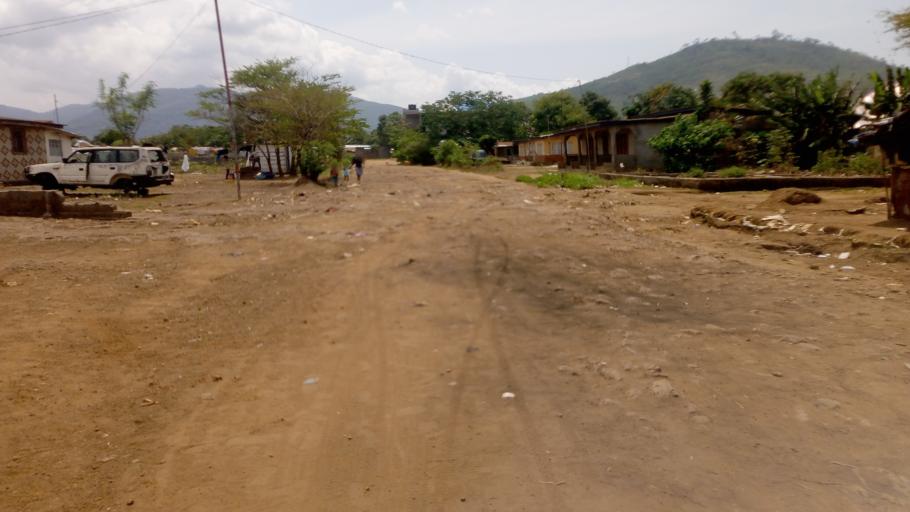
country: SL
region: Western Area
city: Waterloo
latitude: 8.3263
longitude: -13.0773
